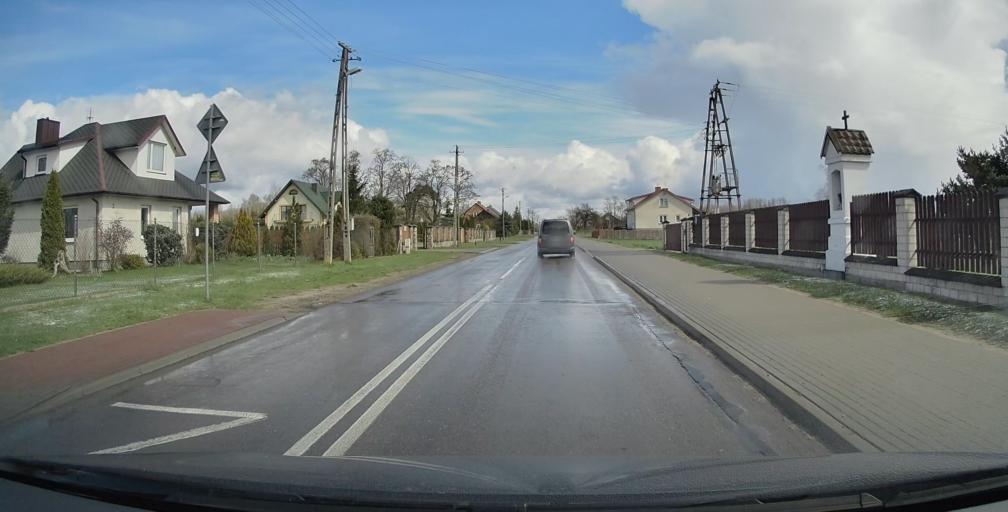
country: PL
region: Masovian Voivodeship
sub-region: Powiat wyszkowski
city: Dlugosiodlo
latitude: 52.6947
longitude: 21.6004
